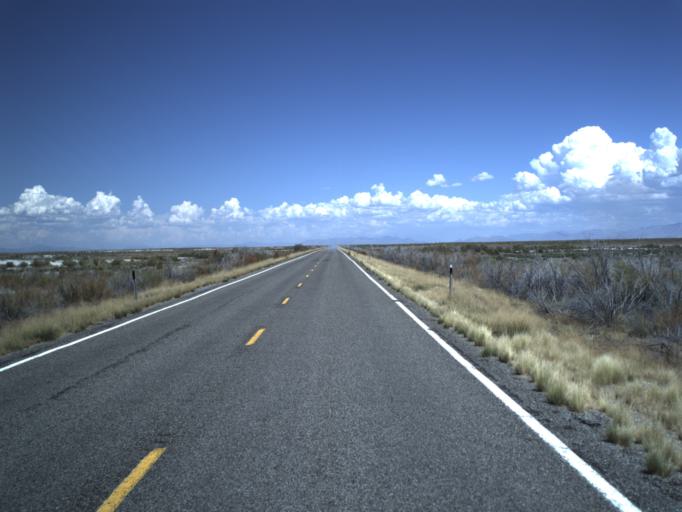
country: US
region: Utah
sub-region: Millard County
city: Delta
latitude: 39.2686
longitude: -112.8660
